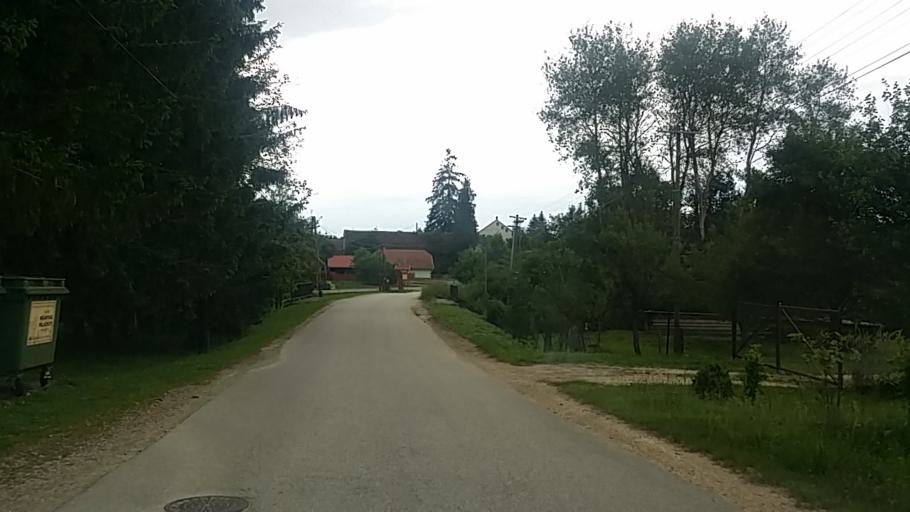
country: SI
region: Hodos-Hodos
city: Hodos
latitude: 46.8471
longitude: 16.4148
